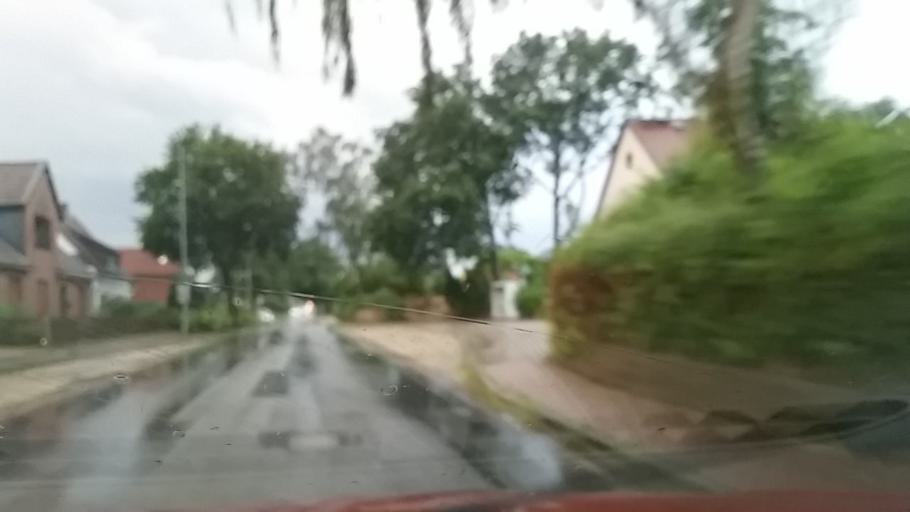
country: DE
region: Lower Saxony
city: Lehre
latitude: 52.3159
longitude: 10.6334
